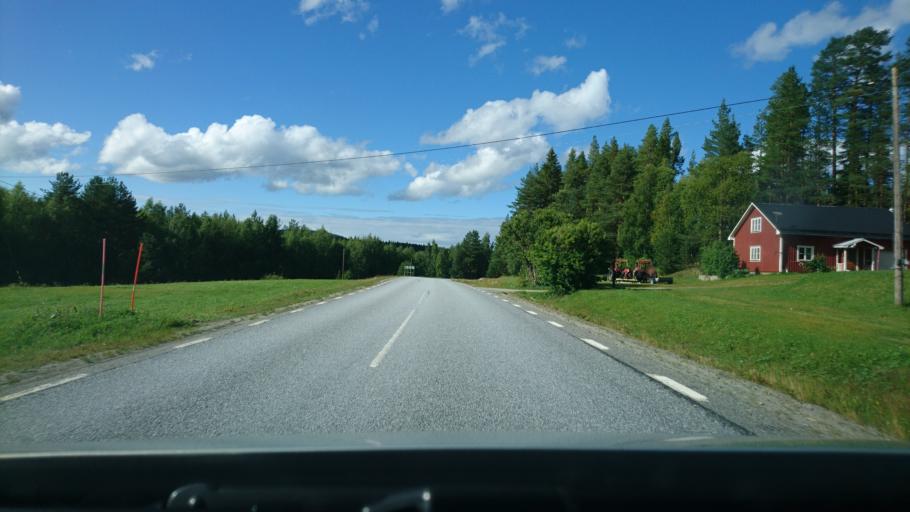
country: SE
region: Vaesterbotten
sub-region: Asele Kommun
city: Asele
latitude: 64.2574
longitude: 17.2708
